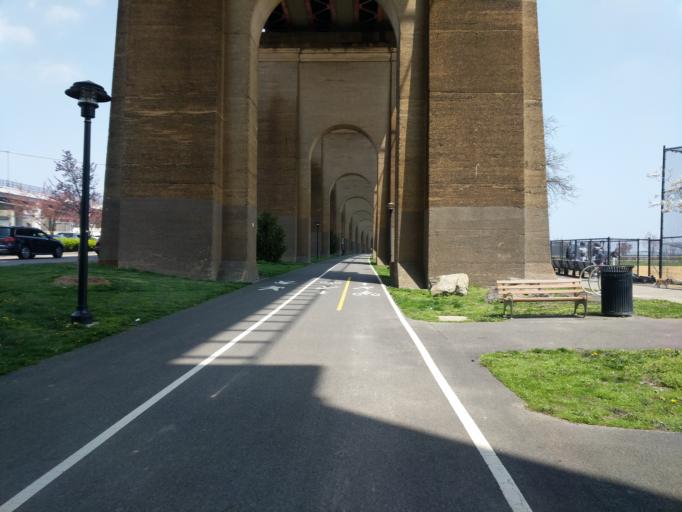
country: US
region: New York
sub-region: New York County
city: Manhattan
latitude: 40.7939
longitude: -73.9211
